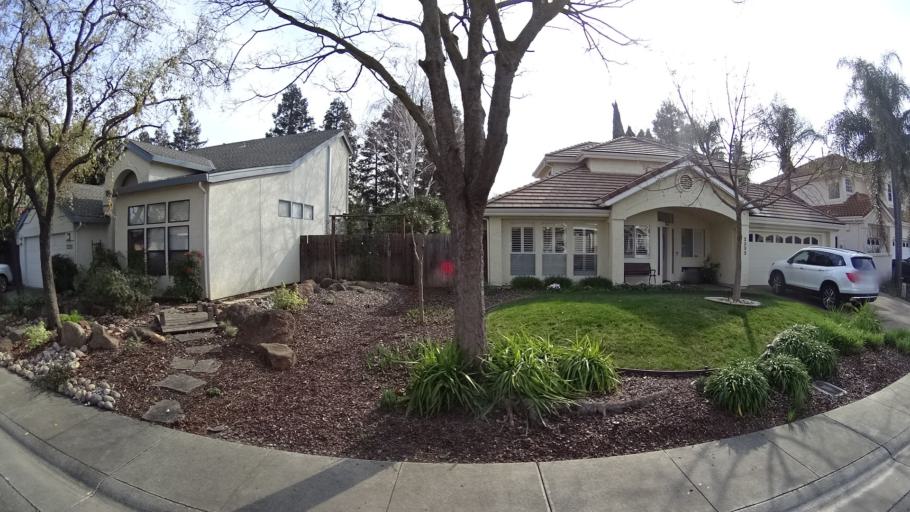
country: US
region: California
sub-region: Yolo County
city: Davis
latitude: 38.5580
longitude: -121.7813
